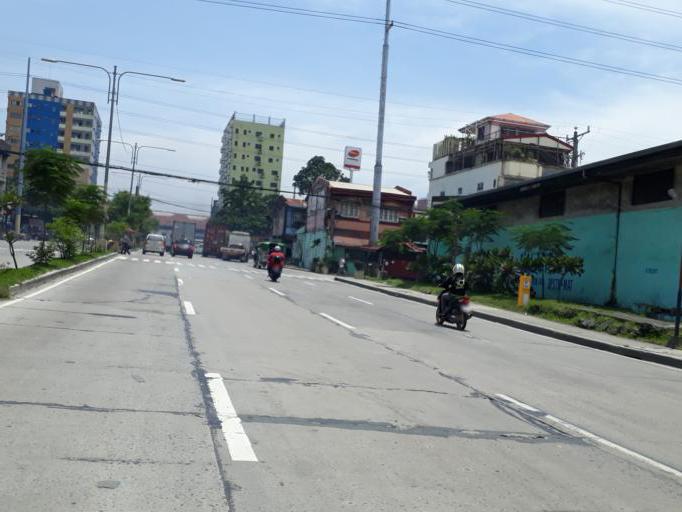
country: PH
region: Metro Manila
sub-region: Caloocan City
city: Niugan
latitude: 14.6447
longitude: 120.9809
